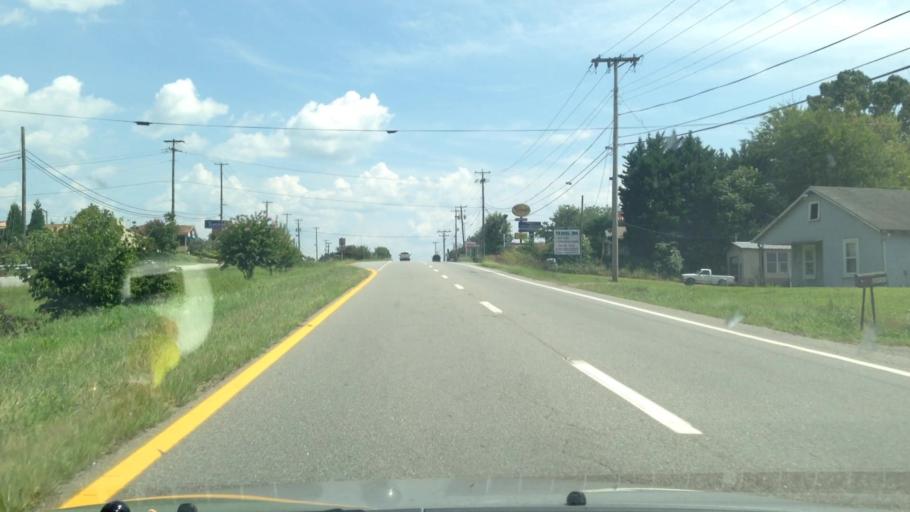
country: US
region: Virginia
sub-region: City of Martinsville
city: Martinsville
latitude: 36.6425
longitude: -79.8630
